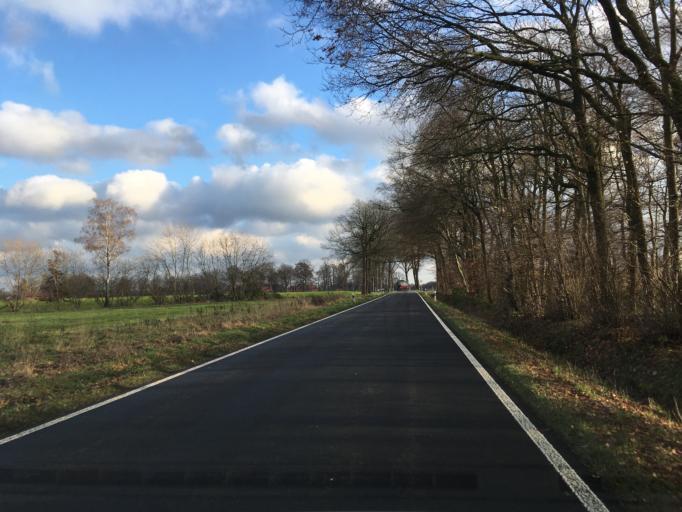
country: DE
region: North Rhine-Westphalia
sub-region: Regierungsbezirk Munster
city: Gescher
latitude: 51.9555
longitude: 7.0364
